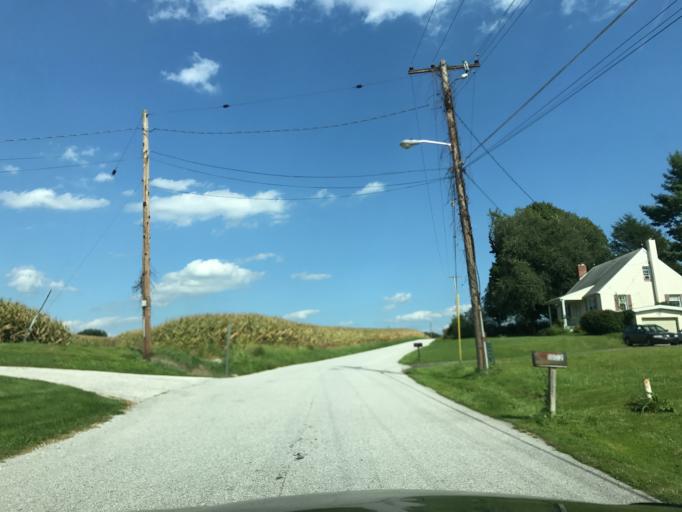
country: US
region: Pennsylvania
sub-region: York County
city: Stewartstown
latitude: 39.6508
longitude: -76.6158
